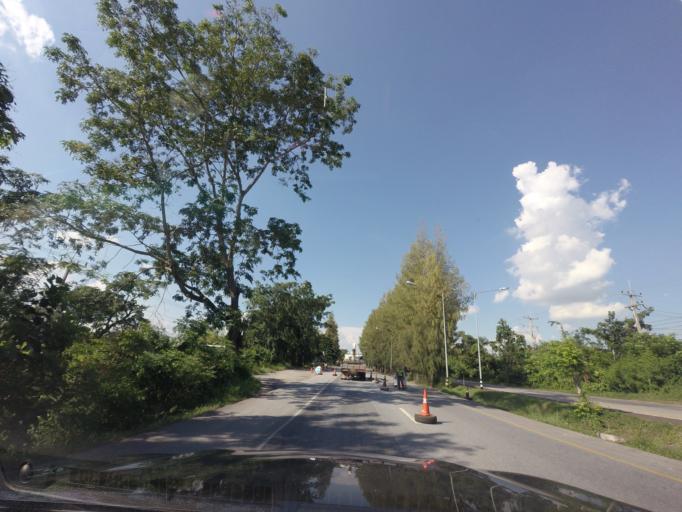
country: TH
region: Nakhon Ratchasima
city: Sida
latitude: 15.5369
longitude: 102.5454
